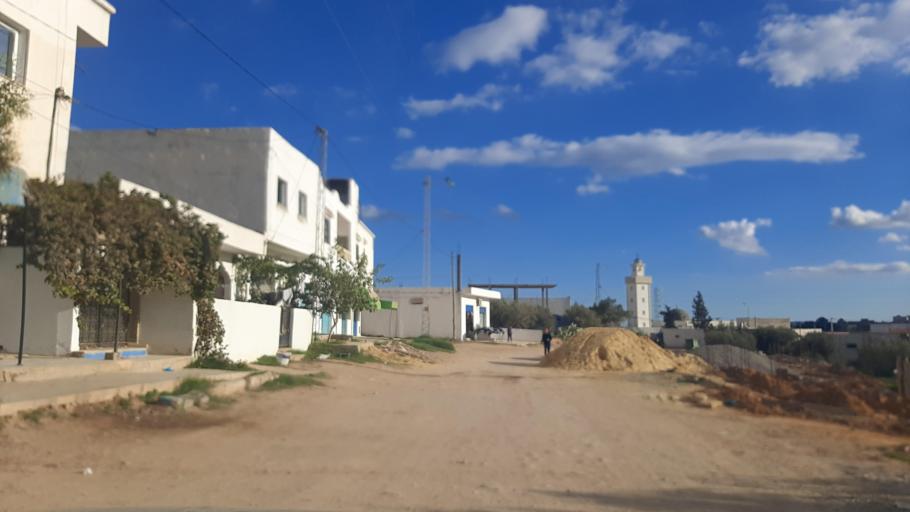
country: TN
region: Nabul
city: Al Hammamat
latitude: 36.4180
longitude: 10.5144
